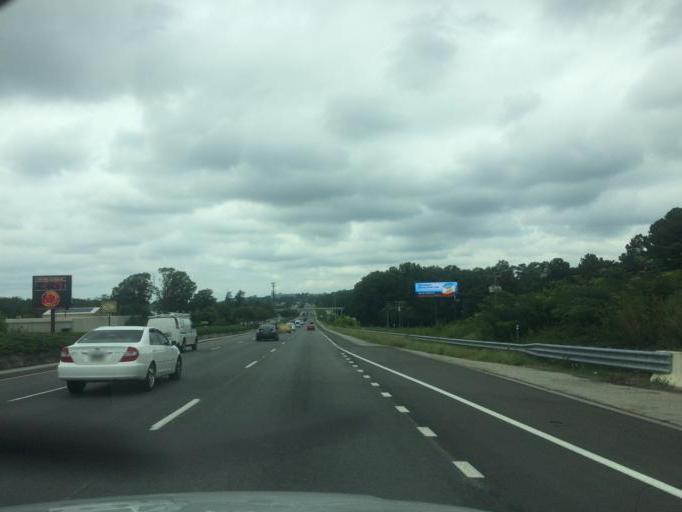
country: US
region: South Carolina
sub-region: Greenville County
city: Wade Hampton
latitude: 34.8444
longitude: -82.3200
